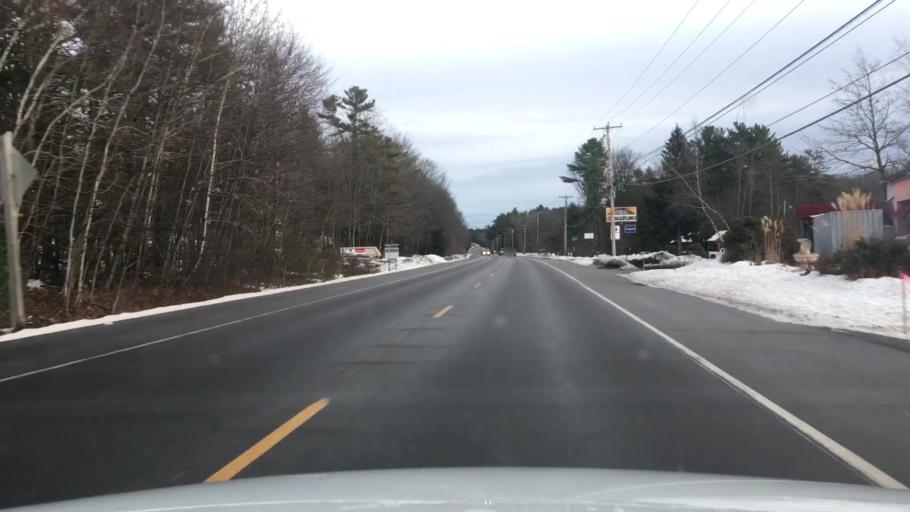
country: US
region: Maine
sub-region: Cumberland County
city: Falmouth Foreside
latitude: 43.7418
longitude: -70.2187
